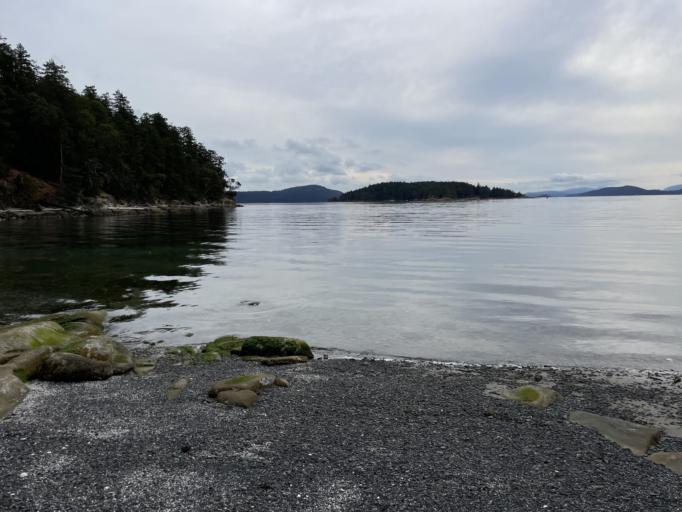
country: CA
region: British Columbia
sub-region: Cowichan Valley Regional District
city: Ladysmith
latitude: 49.0940
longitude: -123.7260
